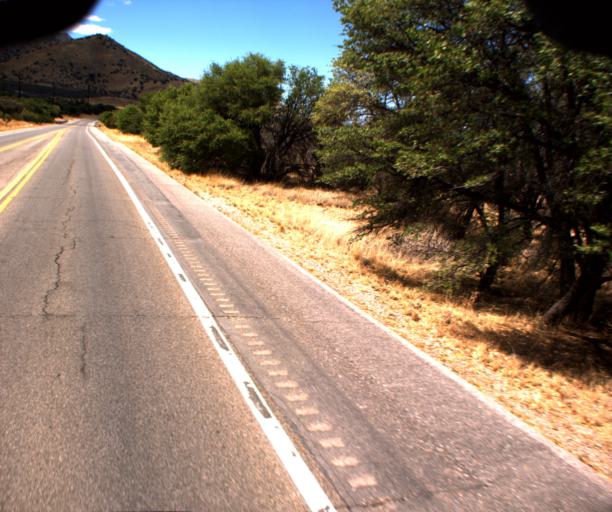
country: US
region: Arizona
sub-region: Cochise County
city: Sierra Vista Southeast
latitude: 31.3950
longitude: -110.2356
